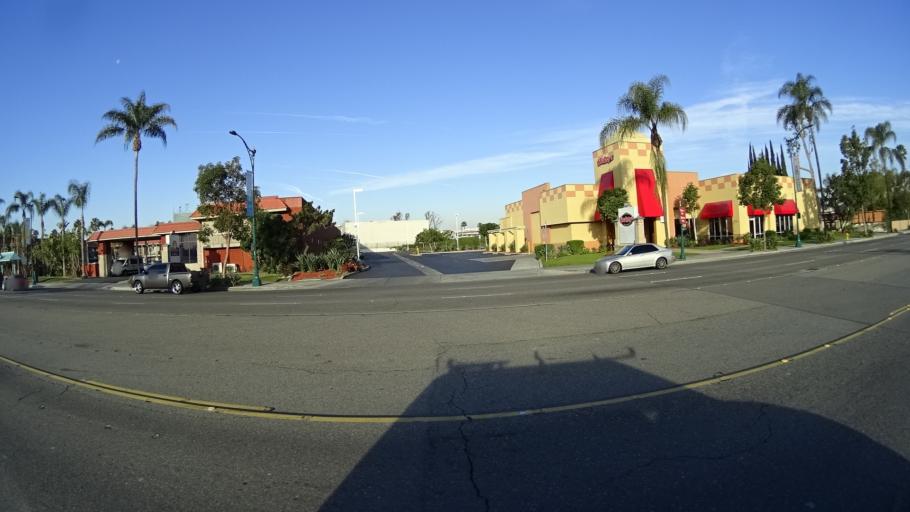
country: US
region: California
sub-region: Orange County
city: Anaheim
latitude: 33.8192
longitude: -117.9153
